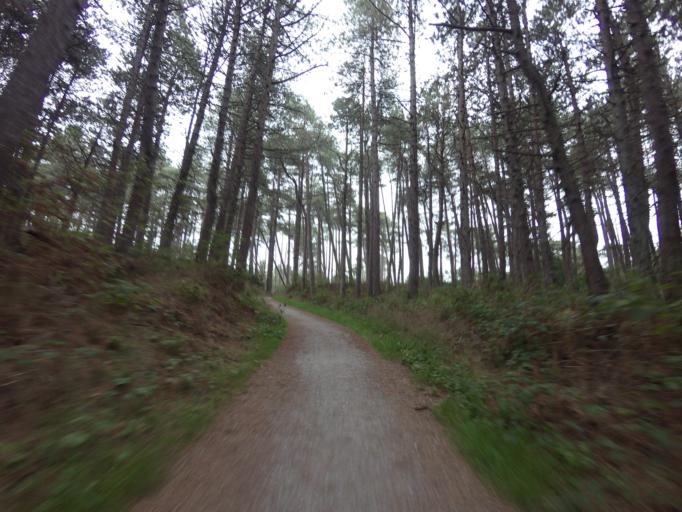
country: NL
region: Friesland
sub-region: Gemeente Schiermonnikoog
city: Schiermonnikoog
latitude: 53.4932
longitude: 6.1681
